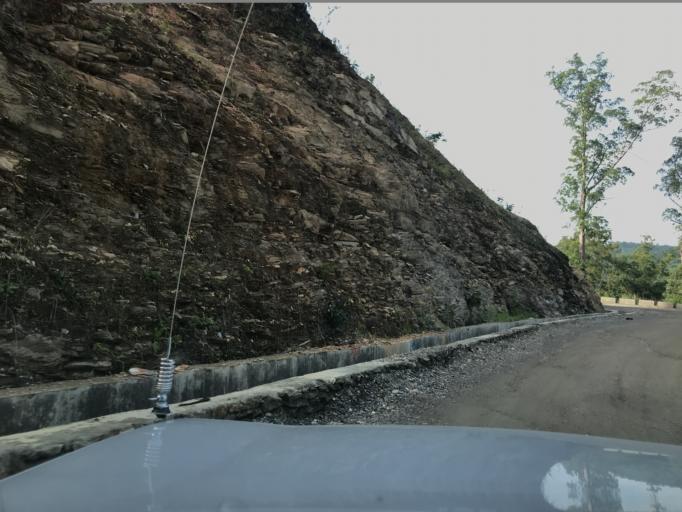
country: TL
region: Aileu
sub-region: Aileu Villa
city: Aileu
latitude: -8.6562
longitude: 125.5275
